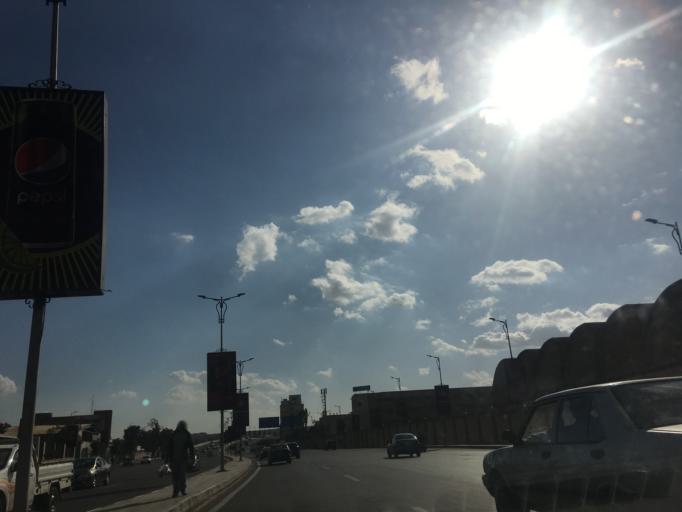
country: EG
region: Muhafazat al Qahirah
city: Cairo
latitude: 30.0480
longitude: 31.3075
